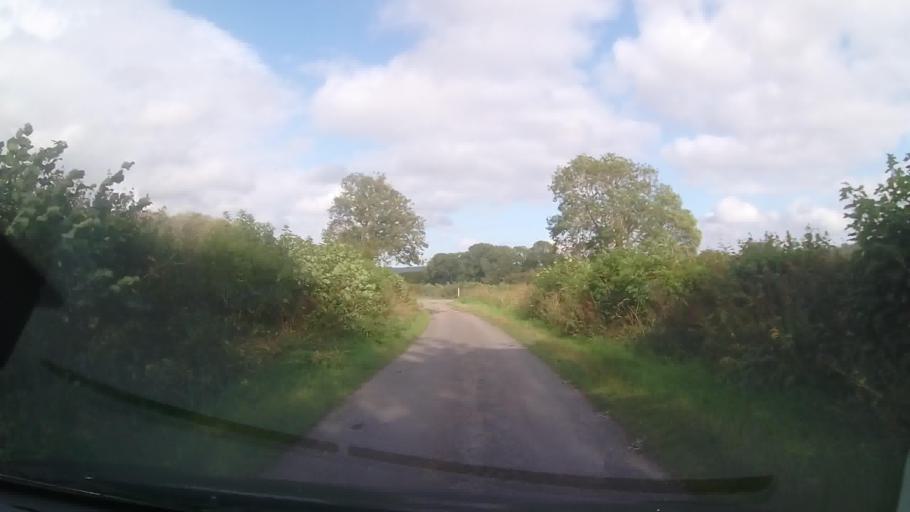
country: GB
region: England
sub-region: Shropshire
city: Lydham
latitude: 52.4950
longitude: -2.9803
